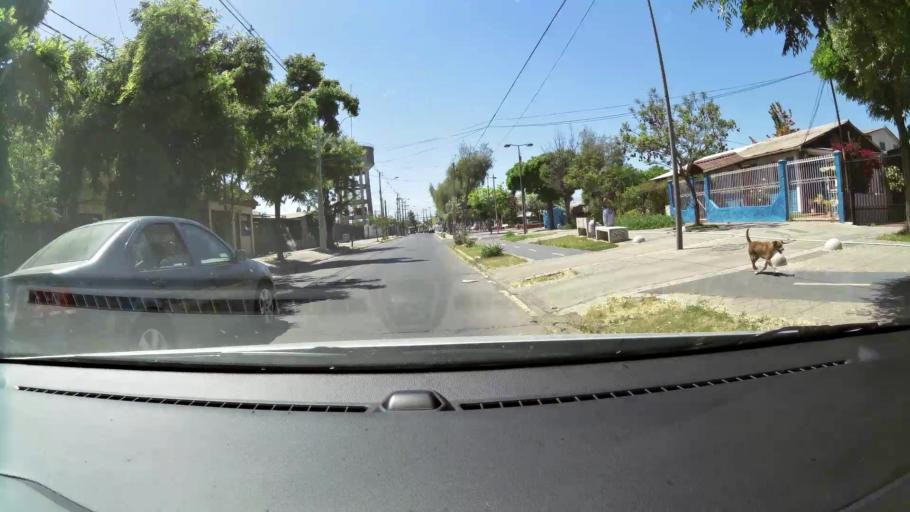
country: CL
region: Santiago Metropolitan
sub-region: Provincia de Maipo
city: San Bernardo
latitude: -33.5709
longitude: -70.6750
